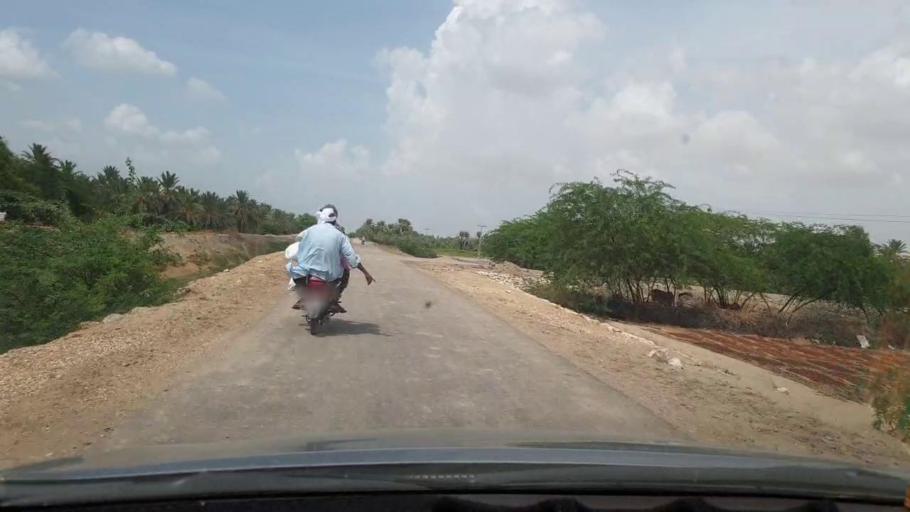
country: PK
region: Sindh
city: Khairpur
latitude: 27.4786
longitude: 68.8540
